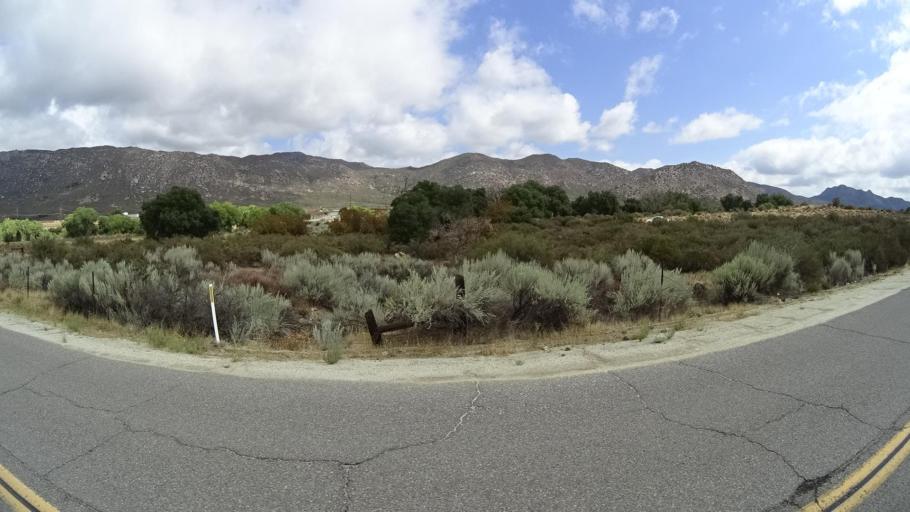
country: US
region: California
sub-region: San Diego County
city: Pine Valley
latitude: 32.7580
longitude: -116.4932
